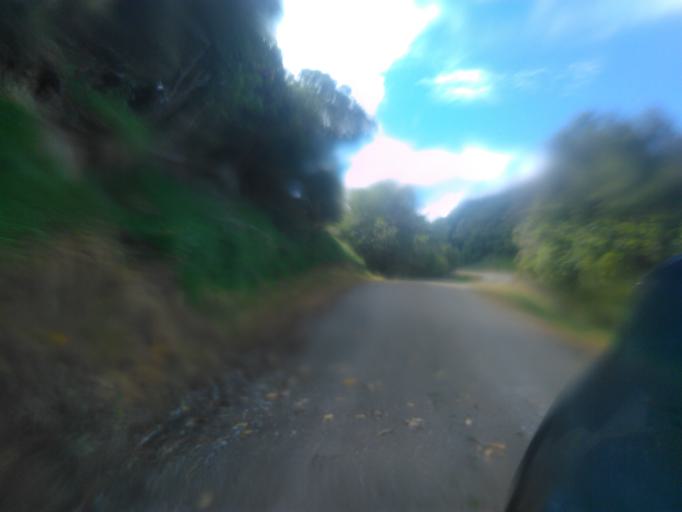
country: NZ
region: Hawke's Bay
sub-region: Wairoa District
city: Wairoa
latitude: -38.7714
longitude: 177.6386
